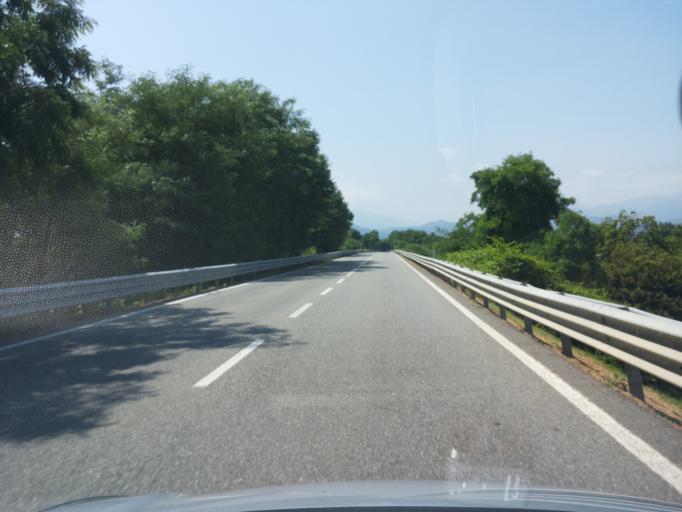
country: IT
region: Piedmont
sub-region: Provincia di Biella
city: Cerreto Castello
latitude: 45.5463
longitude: 8.1750
